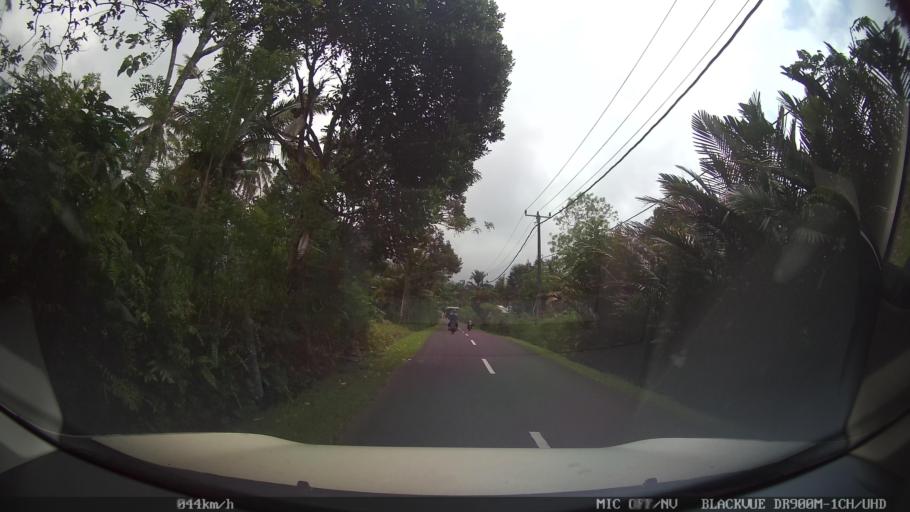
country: ID
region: Bali
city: Banjar Geriana Kangin
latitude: -8.3987
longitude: 115.4407
